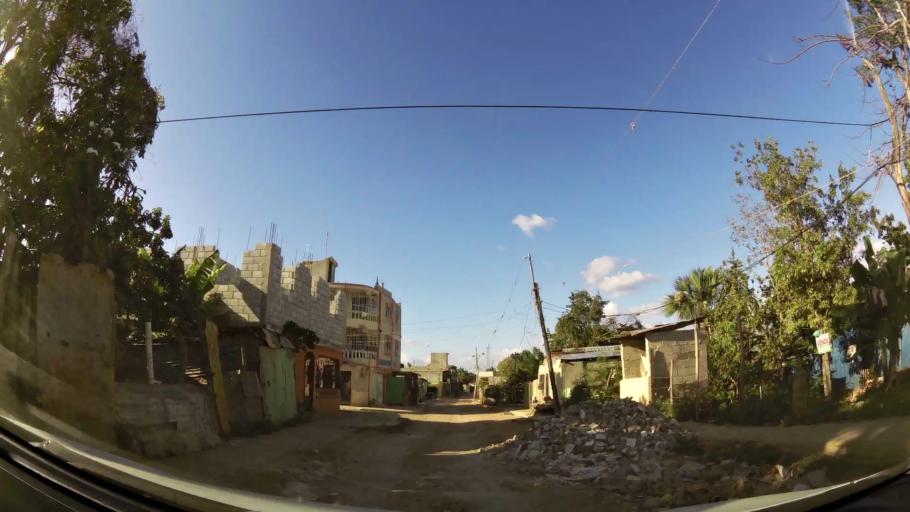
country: DO
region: Santo Domingo
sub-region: Santo Domingo
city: Santo Domingo Este
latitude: 18.4770
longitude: -69.8033
